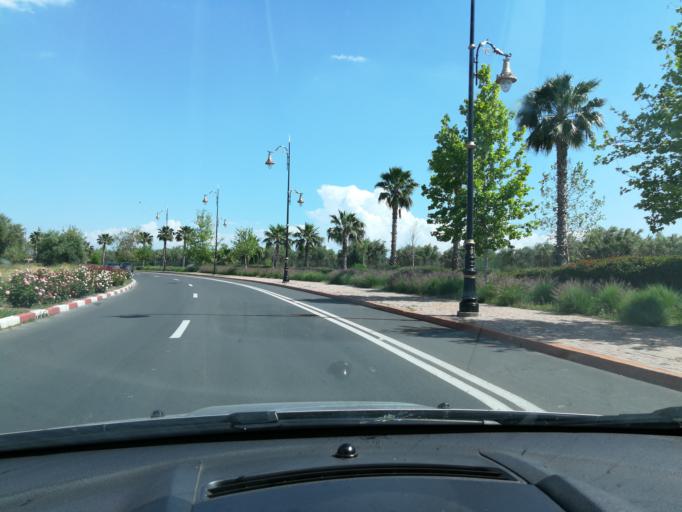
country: MA
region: Marrakech-Tensift-Al Haouz
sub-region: Marrakech
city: Marrakesh
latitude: 31.6131
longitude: -8.0069
